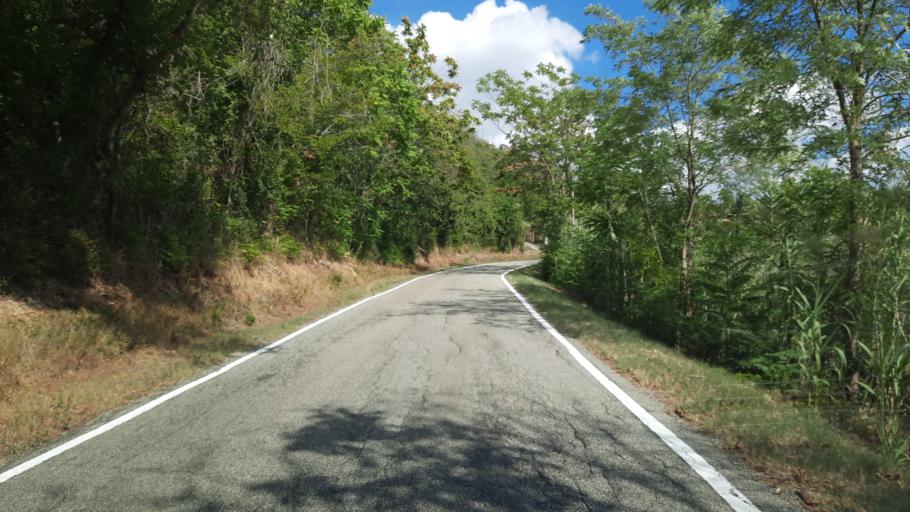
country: IT
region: Piedmont
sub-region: Provincia di Alessandria
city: Cereseto
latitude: 45.0846
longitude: 8.3129
